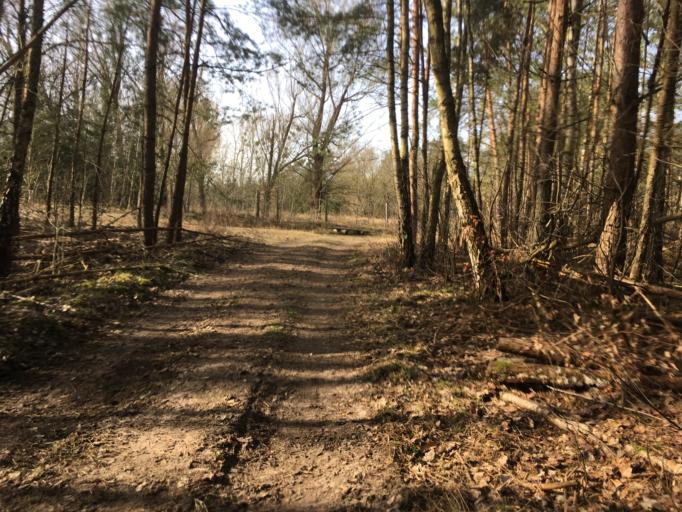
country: DE
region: Brandenburg
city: Bernau bei Berlin
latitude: 52.6960
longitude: 13.5302
